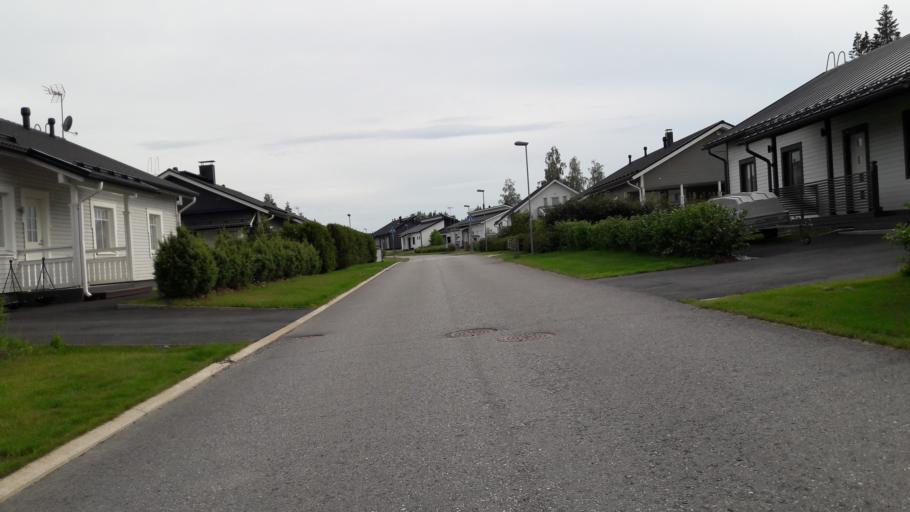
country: FI
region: North Karelia
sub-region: Joensuu
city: Joensuu
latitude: 62.5733
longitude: 29.8214
